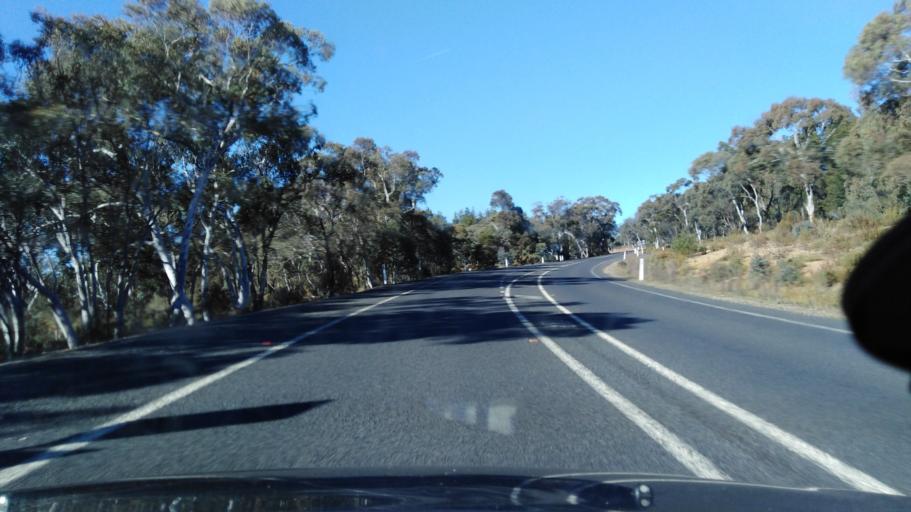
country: AU
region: New South Wales
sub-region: Palerang
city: Bungendore
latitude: -35.1853
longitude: 149.3162
